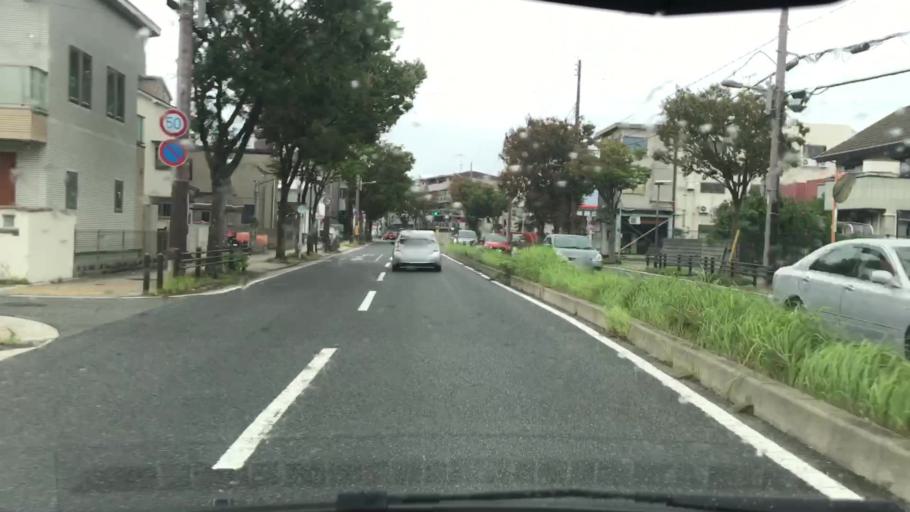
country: JP
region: Hyogo
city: Amagasaki
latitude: 34.7448
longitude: 135.3859
